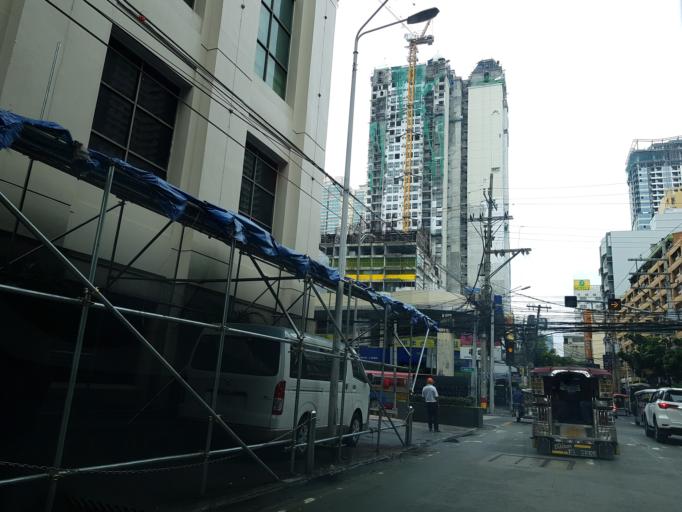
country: PH
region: Metro Manila
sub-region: City of Manila
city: Port Area
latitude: 14.5735
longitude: 120.9832
